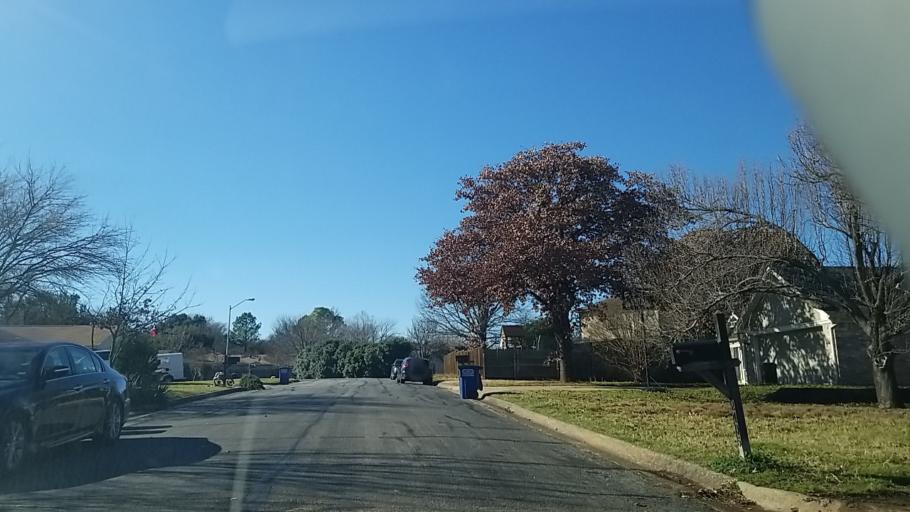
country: US
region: Texas
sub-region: Denton County
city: Corinth
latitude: 33.1555
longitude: -97.0714
